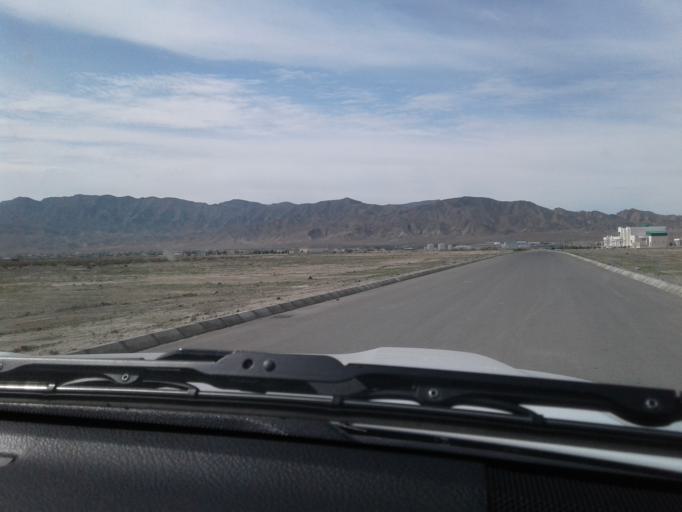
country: TM
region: Balkan
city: Gazanjyk
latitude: 39.2669
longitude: 55.4915
